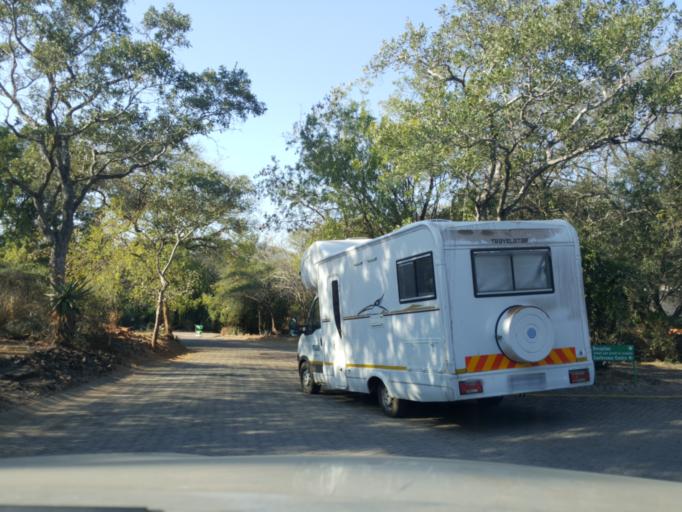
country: SZ
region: Hhohho
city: Ntfonjeni
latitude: -25.4266
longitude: 31.4493
